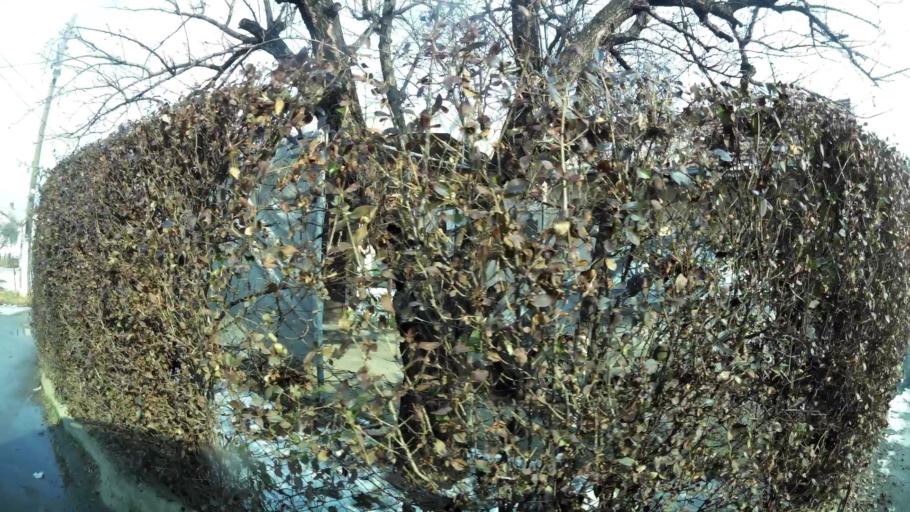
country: MK
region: Kisela Voda
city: Kisela Voda
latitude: 41.9913
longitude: 21.4976
